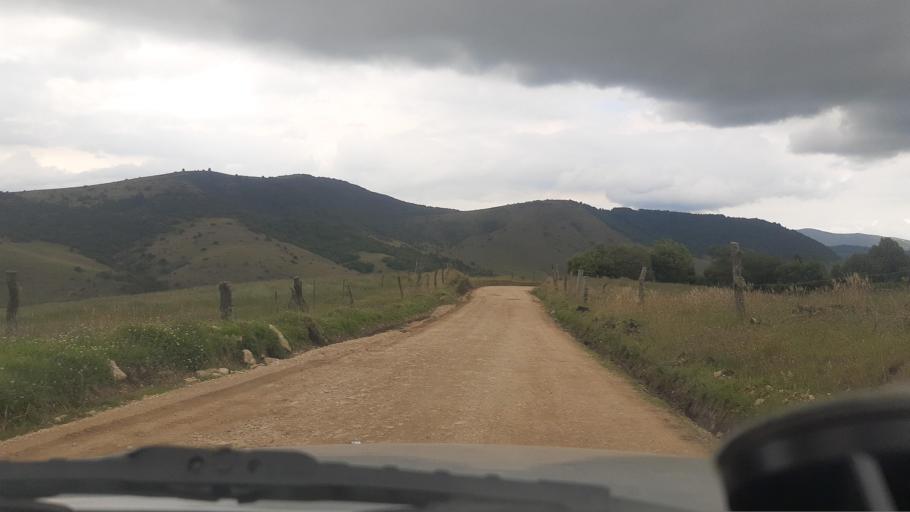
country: CO
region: Cundinamarca
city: Suesca
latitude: 5.1435
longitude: -73.7971
